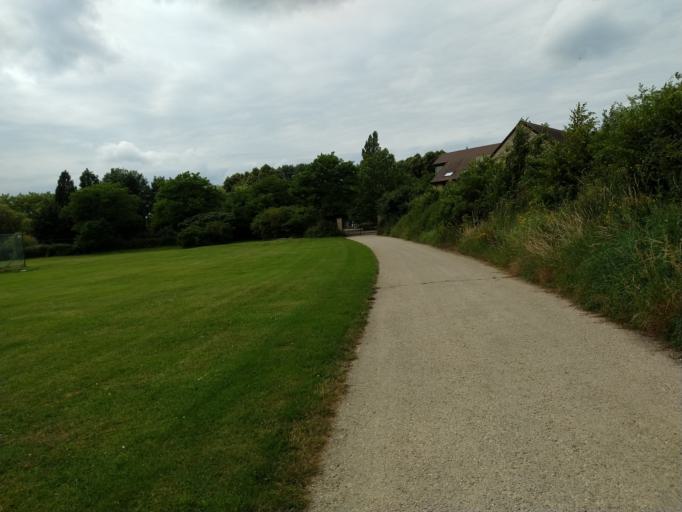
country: BE
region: Flanders
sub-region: Provincie Vlaams-Brabant
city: Diest
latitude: 50.9860
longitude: 5.0655
